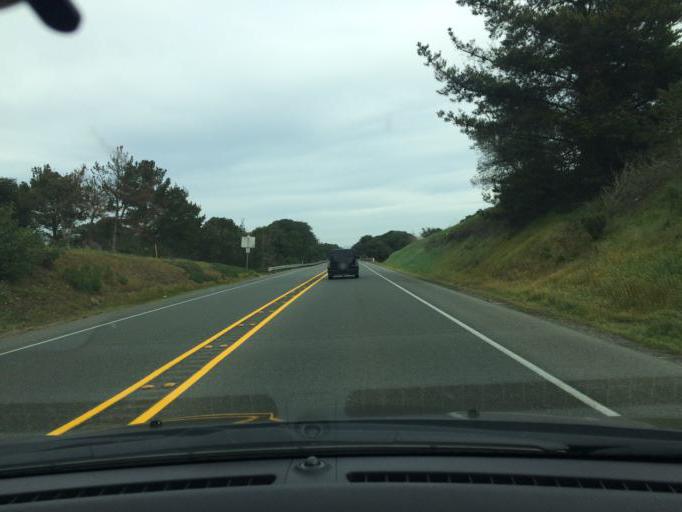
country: US
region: California
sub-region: Monterey County
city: Castroville
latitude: 36.7745
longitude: -121.7223
